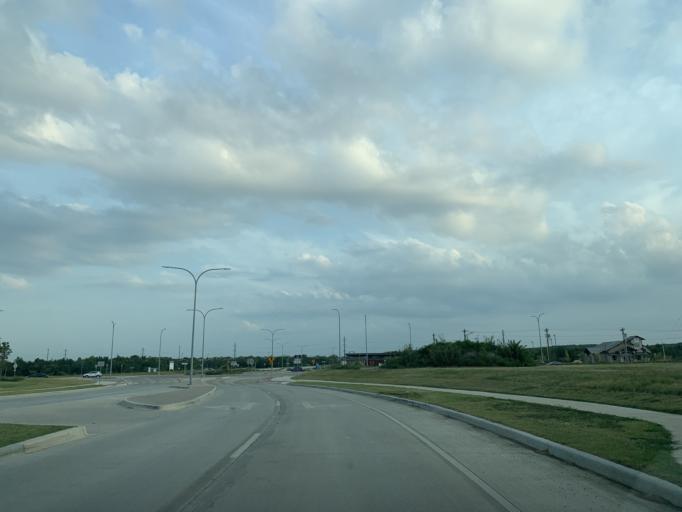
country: US
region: Texas
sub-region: Tarrant County
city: Keller
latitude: 32.9328
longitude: -97.2724
